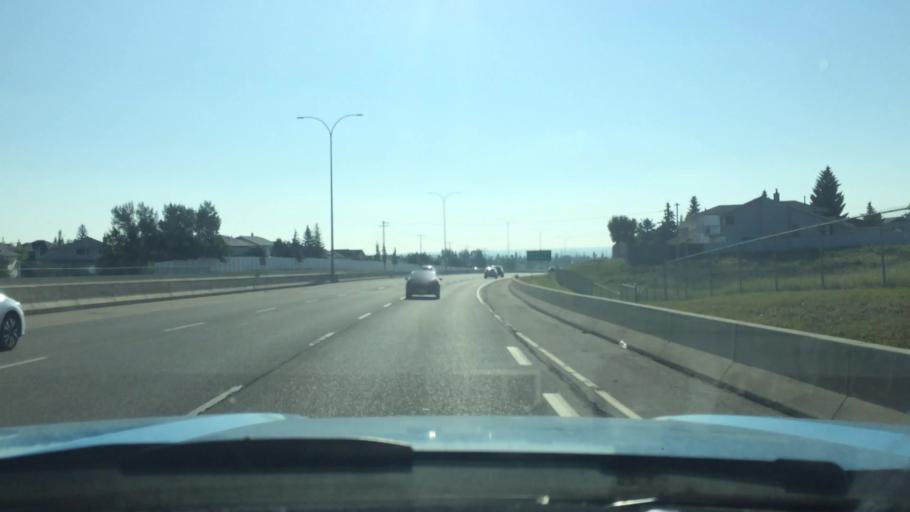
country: CA
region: Alberta
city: Calgary
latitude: 51.1442
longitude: -114.1160
